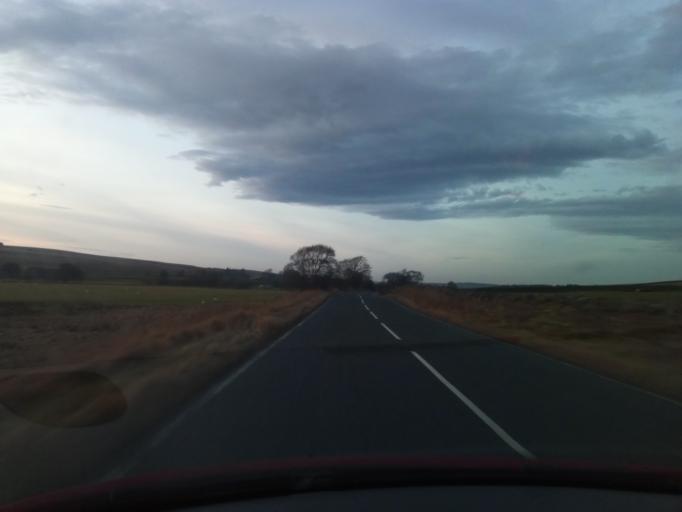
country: GB
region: England
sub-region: Northumberland
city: Otterburn
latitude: 55.2409
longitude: -2.2108
